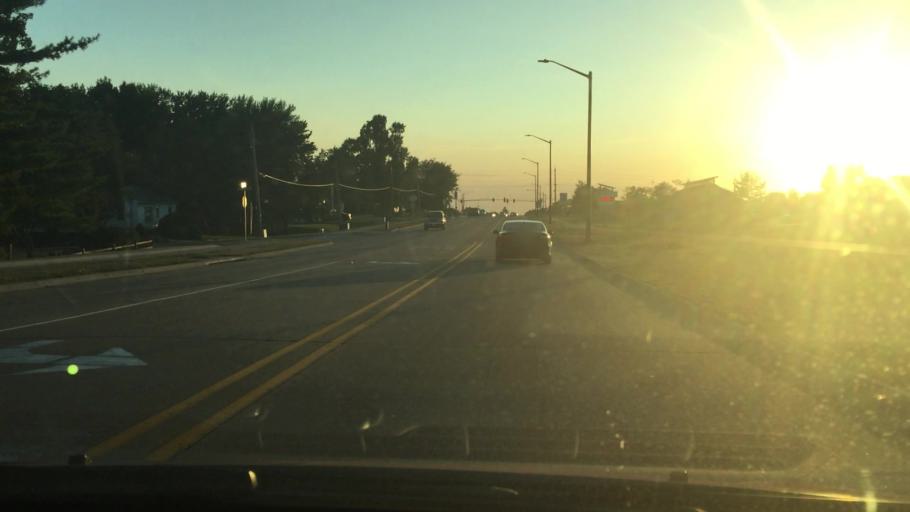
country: US
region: Iowa
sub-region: Muscatine County
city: Muscatine
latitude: 41.4359
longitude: -91.0754
